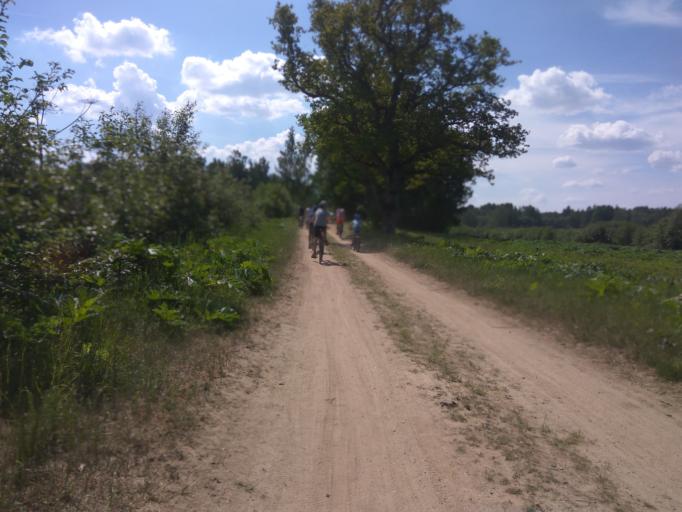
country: LV
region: Kuldigas Rajons
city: Kuldiga
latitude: 56.9341
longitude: 21.9751
